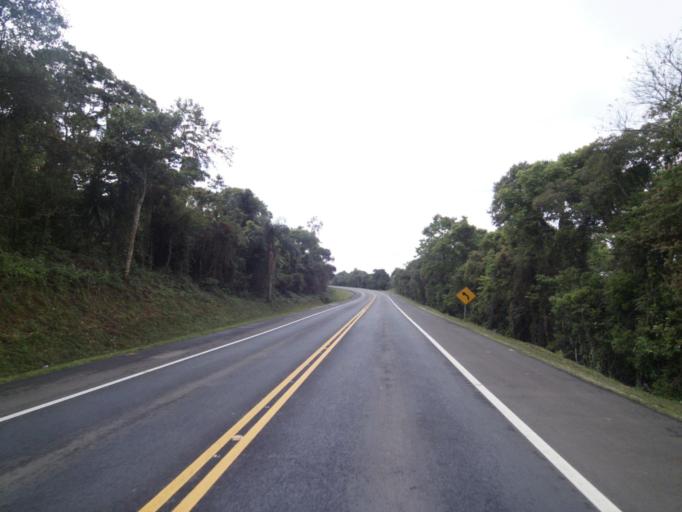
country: BR
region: Parana
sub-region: Irati
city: Irati
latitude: -25.4527
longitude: -50.6459
